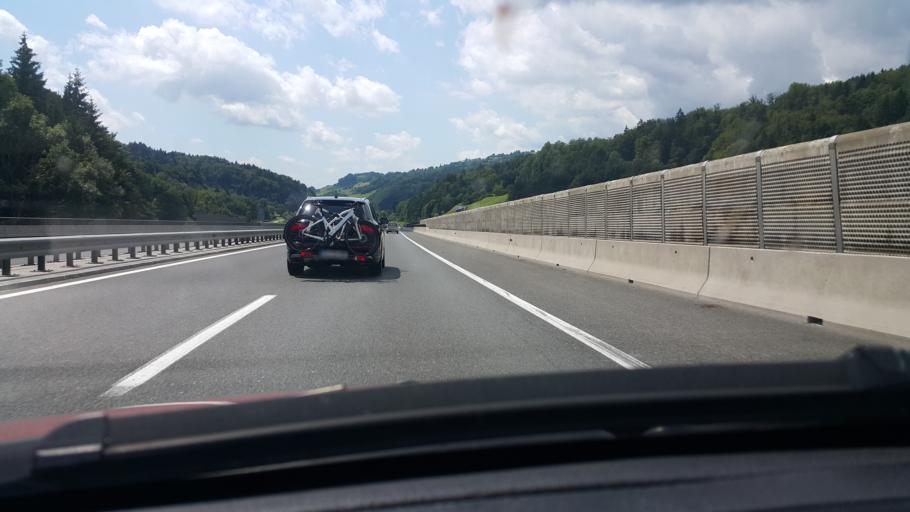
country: SI
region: Moravce
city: Moravce
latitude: 46.1743
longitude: 14.8035
